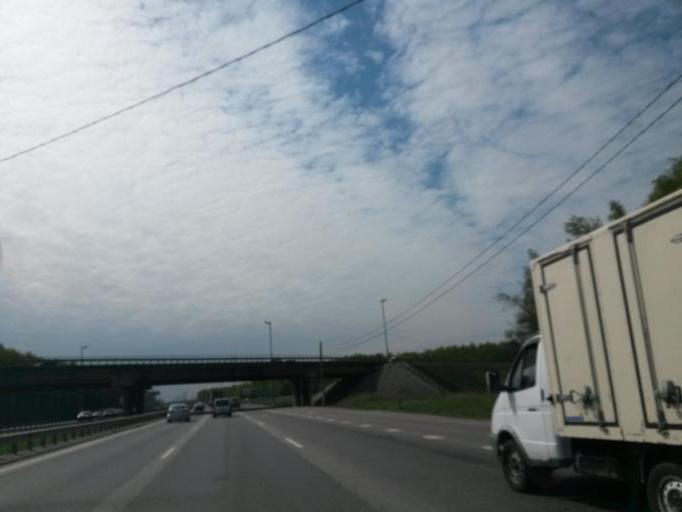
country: RU
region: Moskovskaya
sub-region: Podol'skiy Rayon
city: Podol'sk
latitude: 55.4055
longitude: 37.6056
